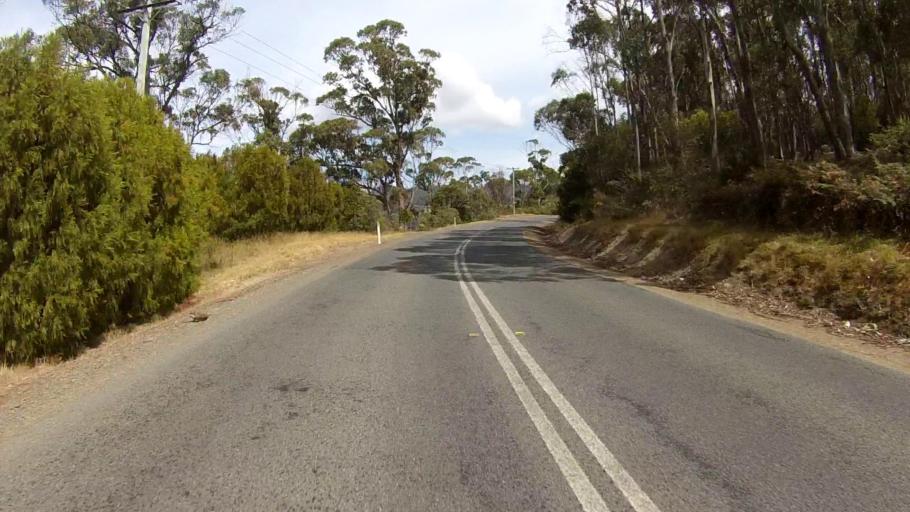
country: AU
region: Tasmania
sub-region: Huon Valley
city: Cygnet
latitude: -43.1831
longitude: 147.0979
